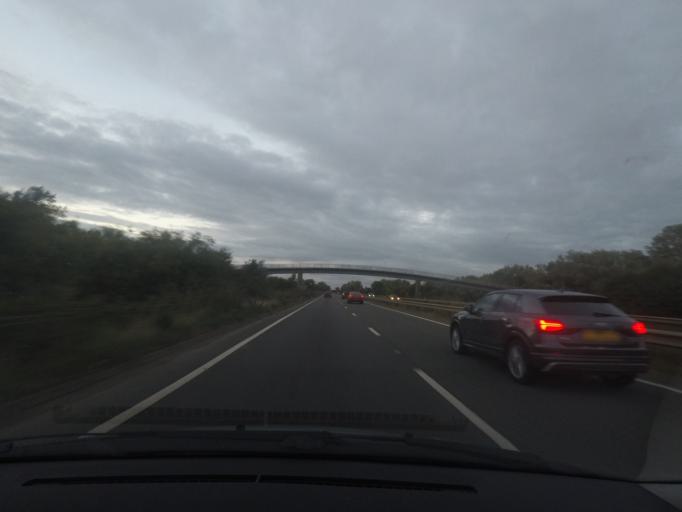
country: GB
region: England
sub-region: Northamptonshire
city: Higham Ferrers
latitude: 52.3085
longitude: -0.6080
